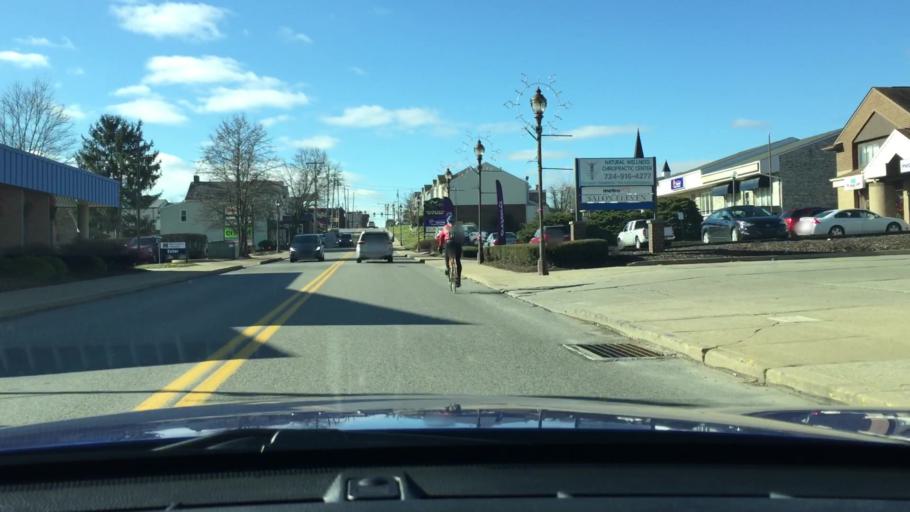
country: US
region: Pennsylvania
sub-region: Washington County
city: Canonsburg
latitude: 40.2598
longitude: -80.1814
